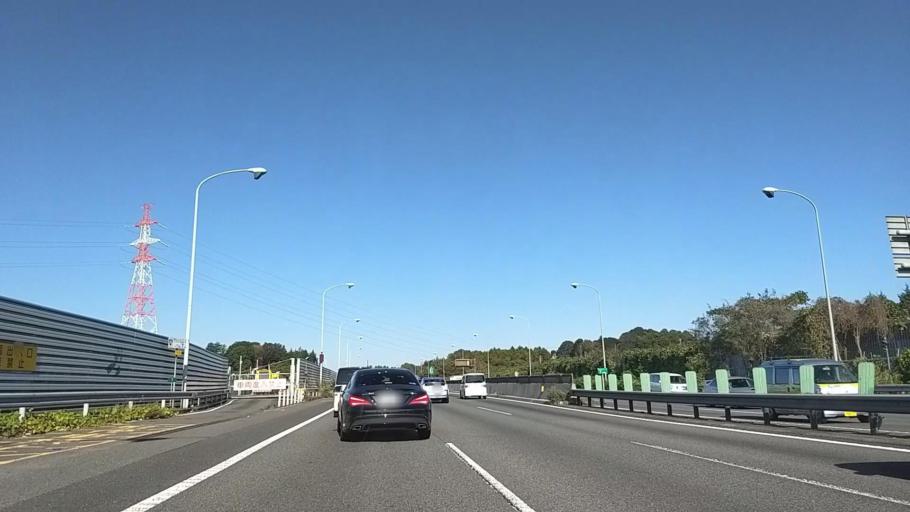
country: JP
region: Kanagawa
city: Minami-rinkan
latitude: 35.4872
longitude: 139.5079
